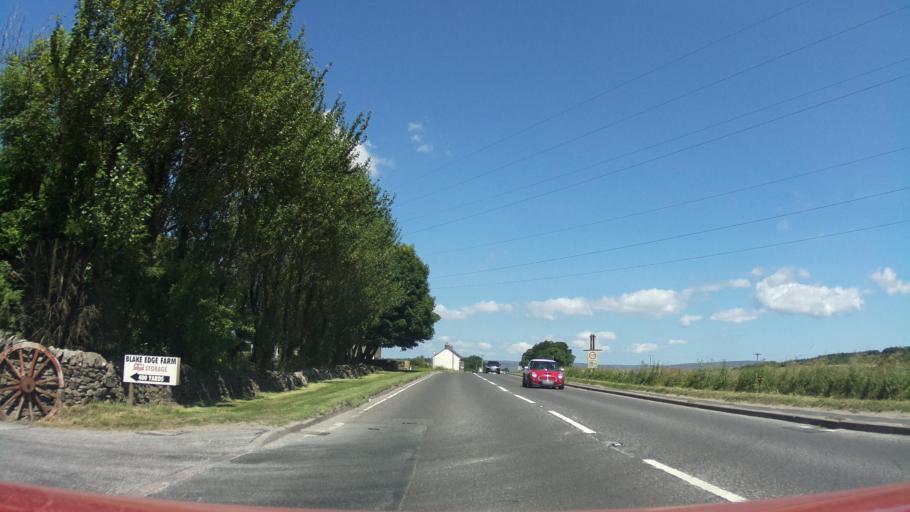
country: GB
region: England
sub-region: Derbyshire
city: Buxton
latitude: 53.2802
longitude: -1.8906
